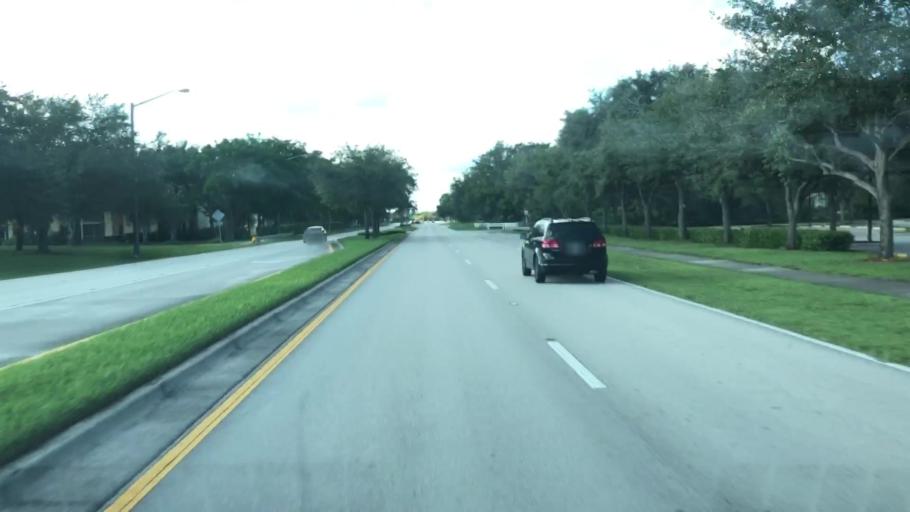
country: US
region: Florida
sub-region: Broward County
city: Coral Springs
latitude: 26.2462
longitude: -80.2690
